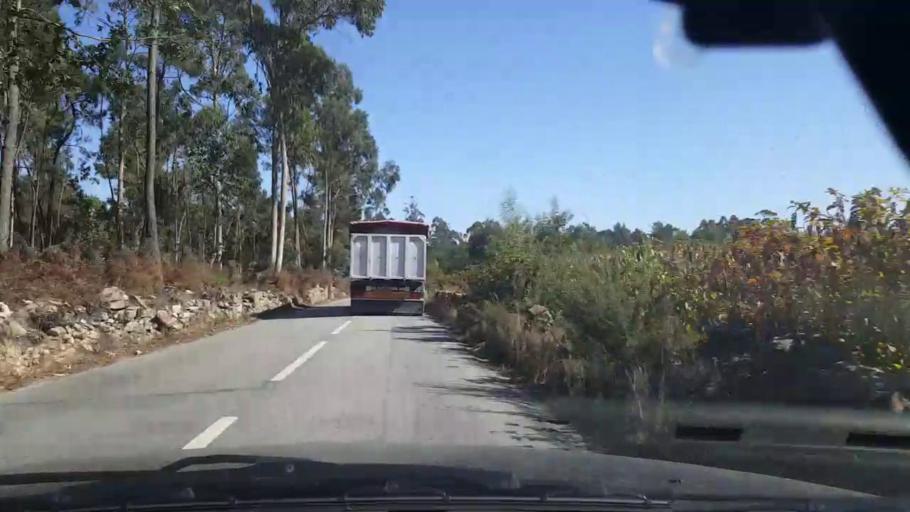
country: PT
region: Braga
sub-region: Vila Nova de Famalicao
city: Ribeirao
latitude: 41.3612
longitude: -8.6286
